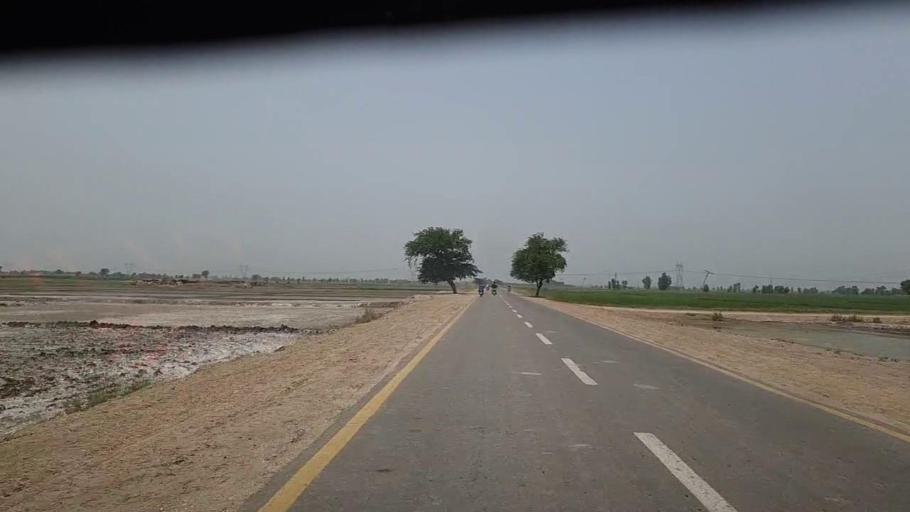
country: PK
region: Sindh
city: Sita Road
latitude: 27.0406
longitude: 67.8784
